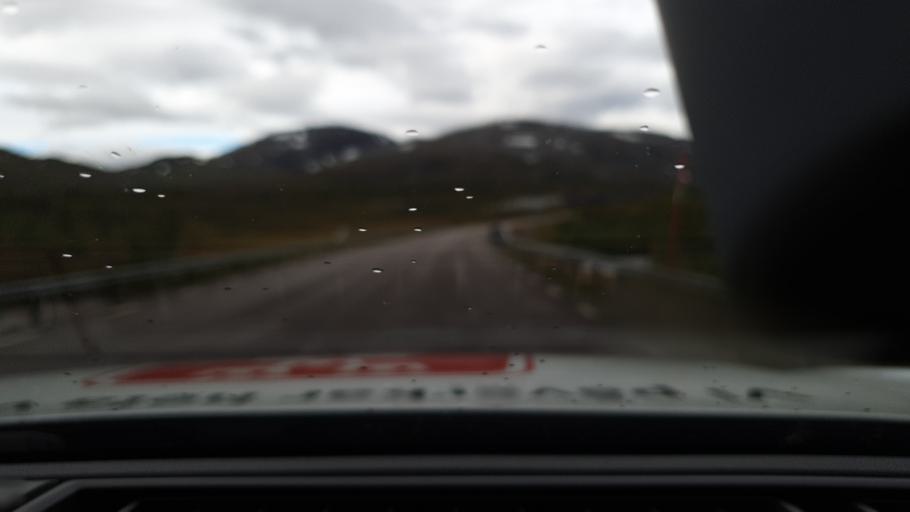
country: NO
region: Troms
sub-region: Bardu
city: Setermoen
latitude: 68.4271
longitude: 18.1854
